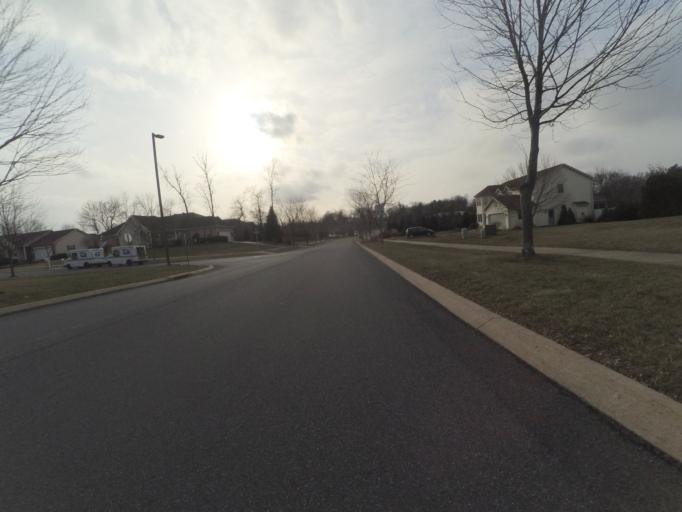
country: US
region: Pennsylvania
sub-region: Centre County
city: Park Forest Village
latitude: 40.7869
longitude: -77.8999
